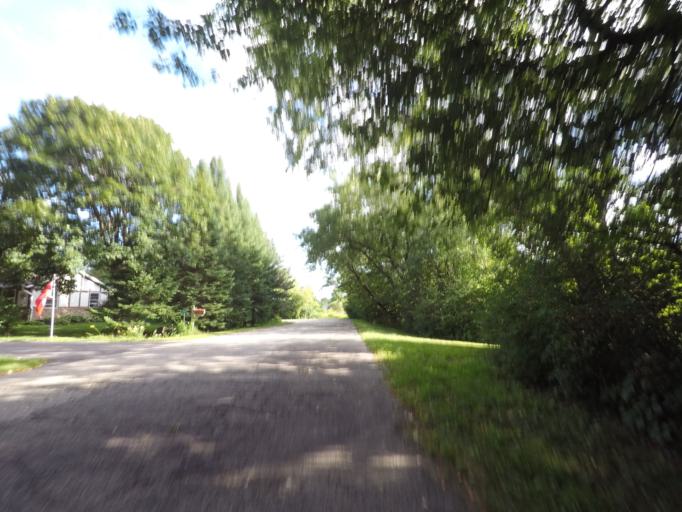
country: US
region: Wisconsin
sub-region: Dane County
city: Middleton
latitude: 43.0734
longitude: -89.5345
